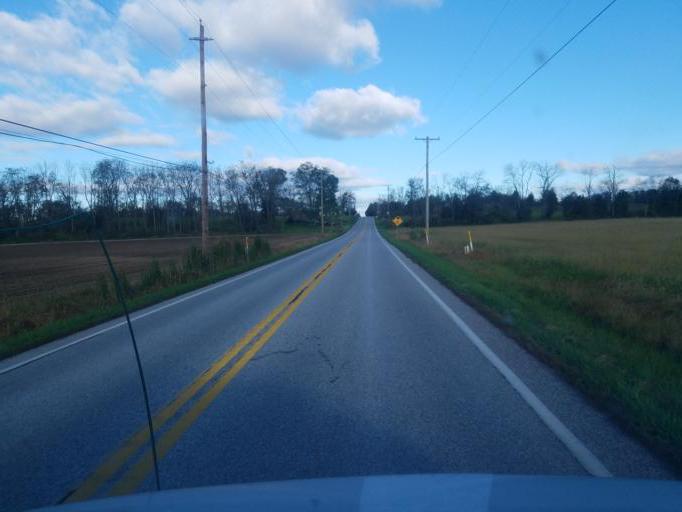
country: US
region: Pennsylvania
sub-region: Adams County
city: Gettysburg
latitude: 39.8527
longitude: -77.2517
